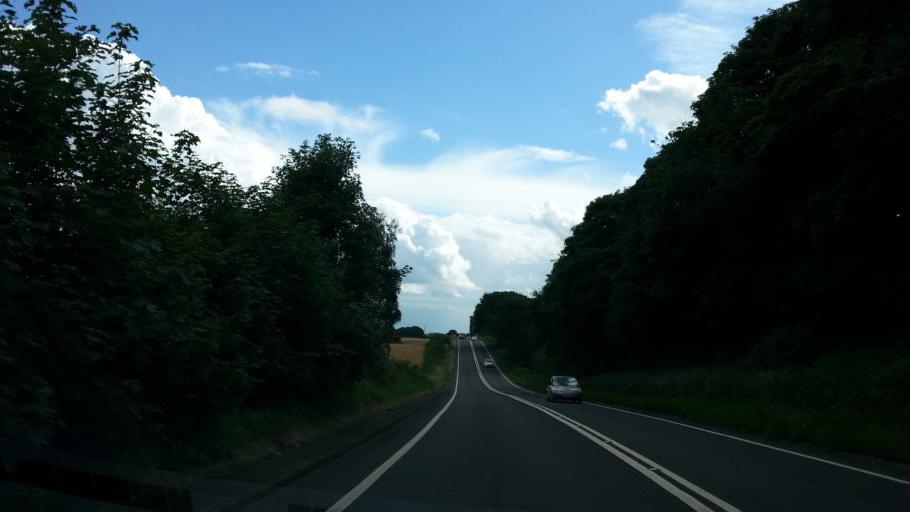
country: GB
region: England
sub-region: Nottinghamshire
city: Bilsthorpe
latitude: 53.1669
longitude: -1.0454
